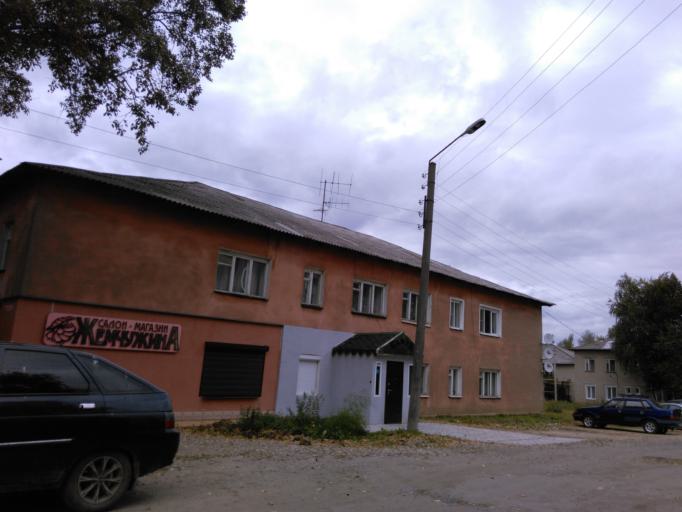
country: RU
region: Ivanovo
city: Privolzhsk
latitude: 57.3794
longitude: 41.2994
